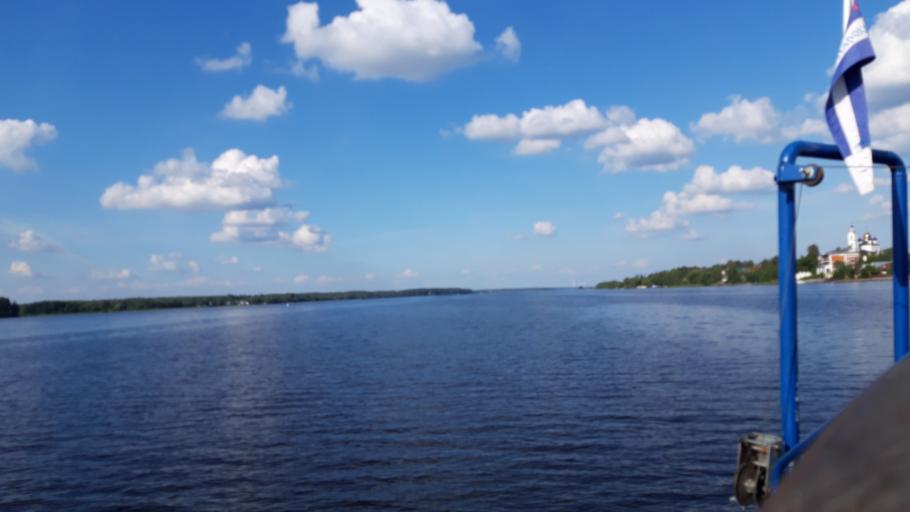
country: RU
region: Tverskaya
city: Zavidovo
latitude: 56.6299
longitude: 36.6035
